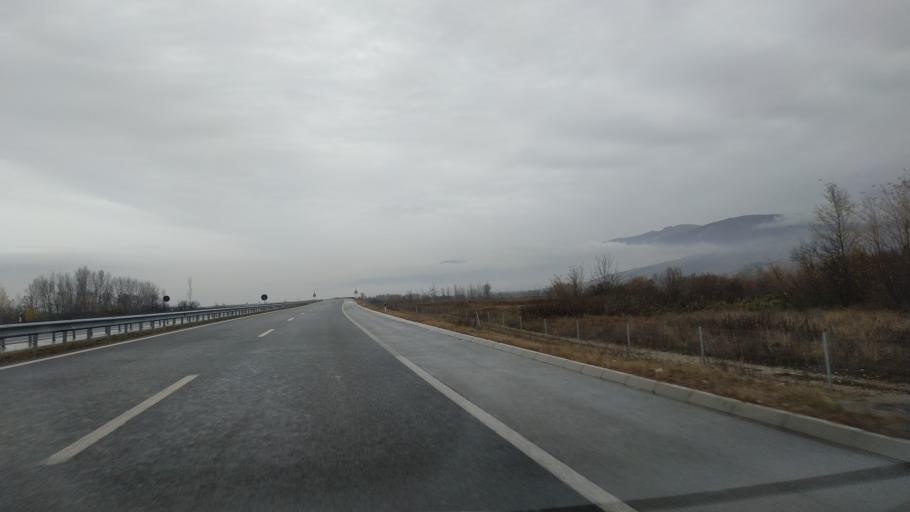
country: RS
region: Central Serbia
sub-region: Pirotski Okrug
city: Dimitrovgrad
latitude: 43.0650
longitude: 22.6800
